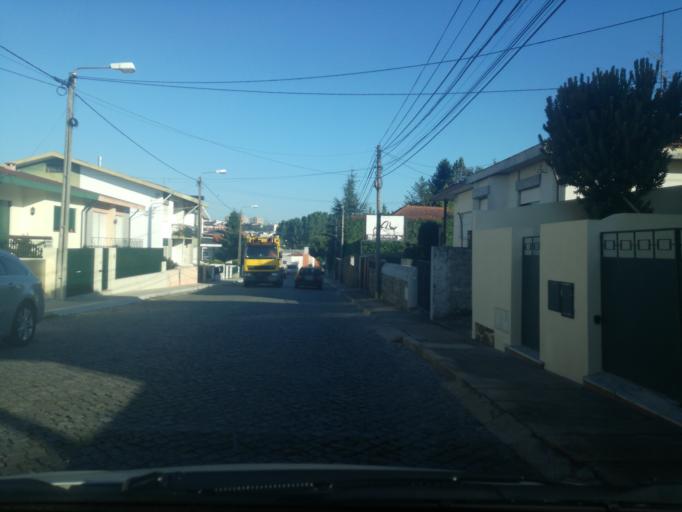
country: PT
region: Porto
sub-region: Maia
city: Milheiros
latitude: 41.2146
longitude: -8.5954
